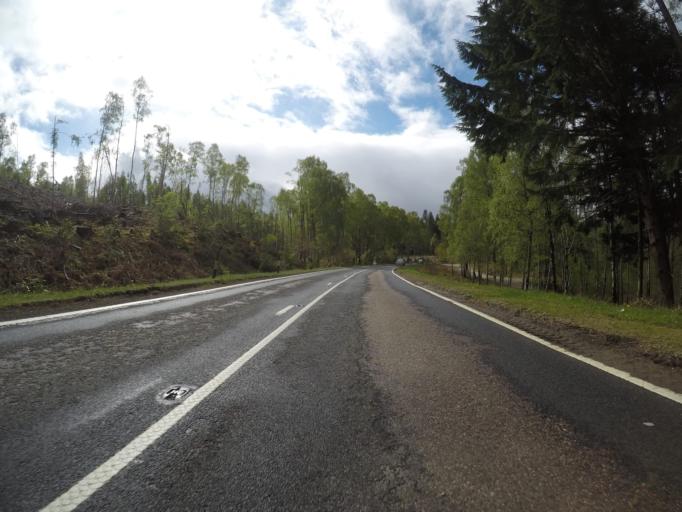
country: GB
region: Scotland
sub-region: Highland
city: Spean Bridge
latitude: 57.0709
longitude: -4.8312
